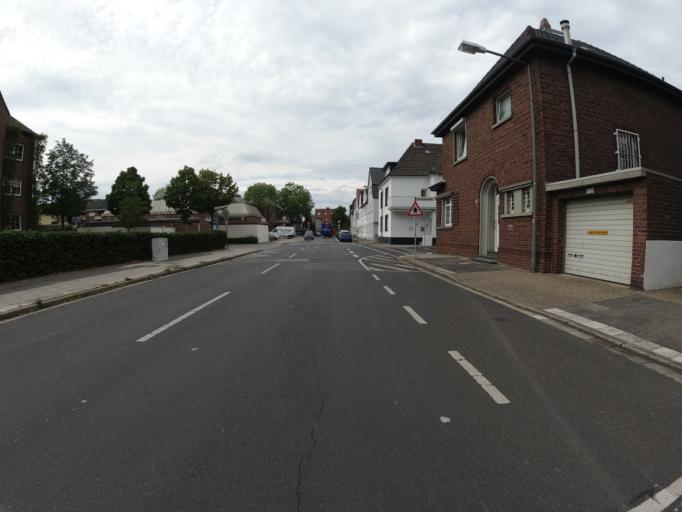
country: DE
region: North Rhine-Westphalia
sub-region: Regierungsbezirk Dusseldorf
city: Moers
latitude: 51.4432
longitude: 6.6266
